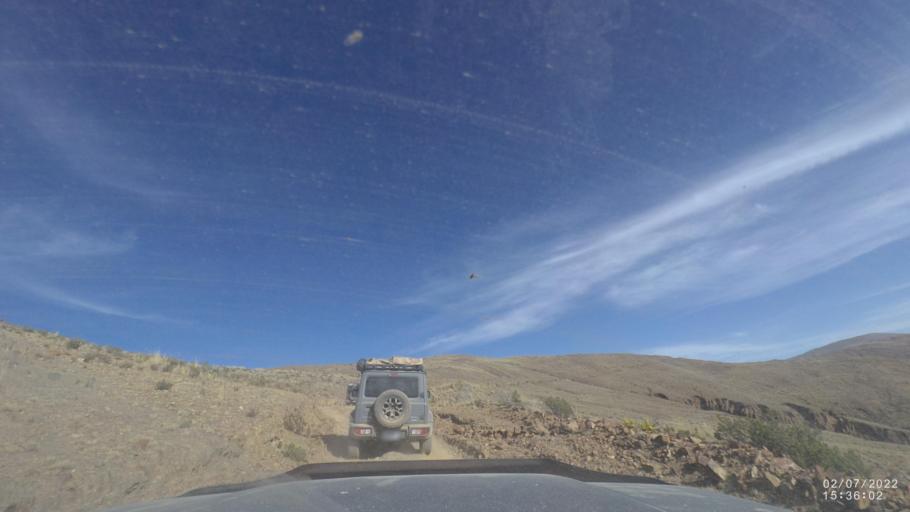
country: BO
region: Cochabamba
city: Irpa Irpa
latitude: -17.8895
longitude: -66.4107
